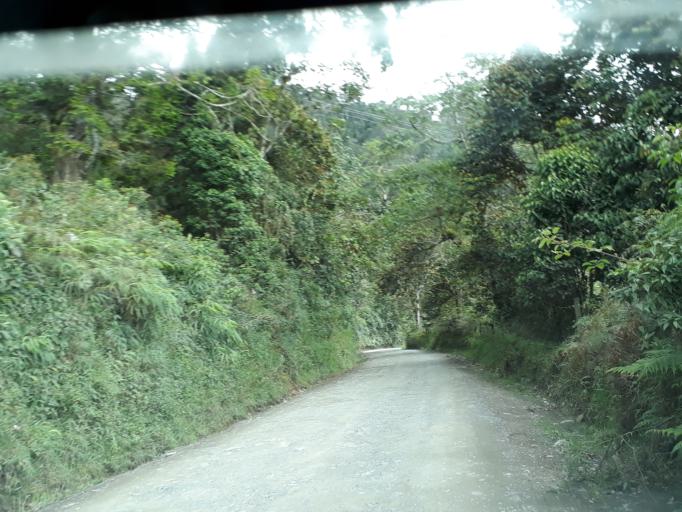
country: CO
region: Cundinamarca
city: Pacho
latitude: 5.2374
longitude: -74.1868
